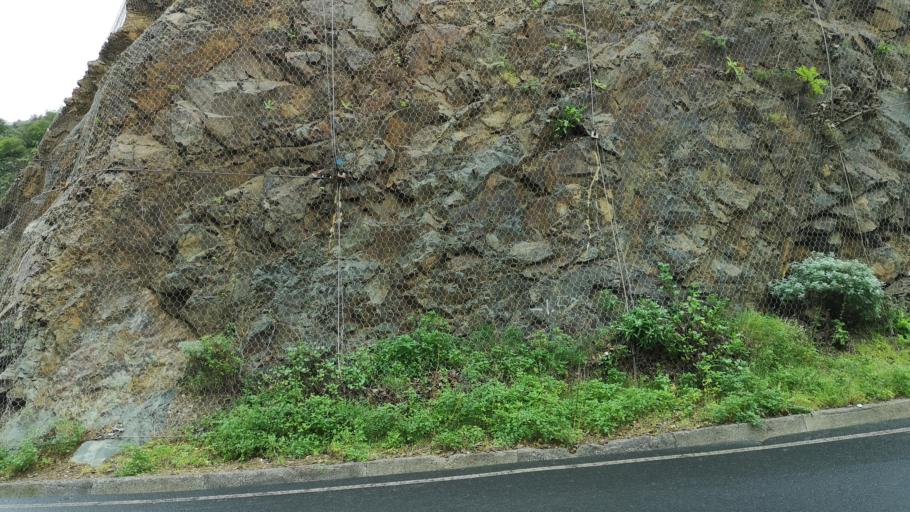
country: ES
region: Canary Islands
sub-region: Provincia de Santa Cruz de Tenerife
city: Agulo
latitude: 28.1883
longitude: -17.2170
